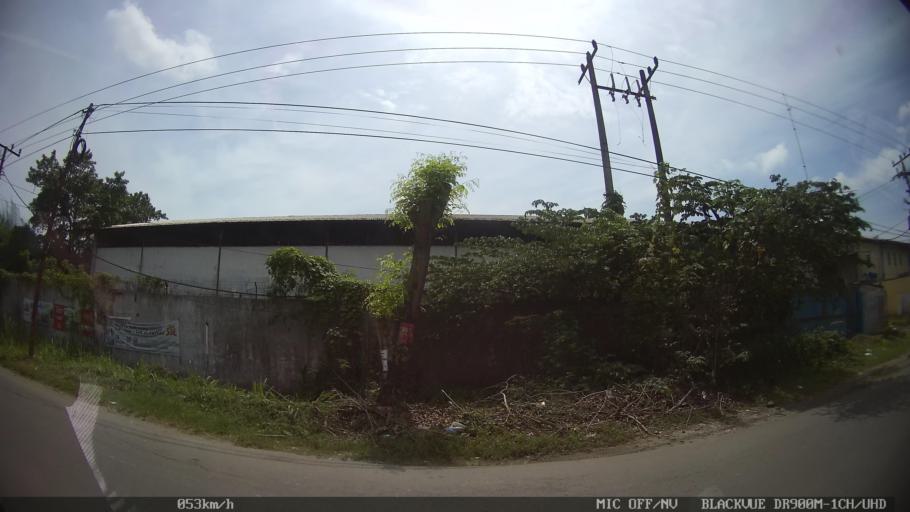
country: ID
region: North Sumatra
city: Medan
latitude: 3.6464
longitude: 98.7169
